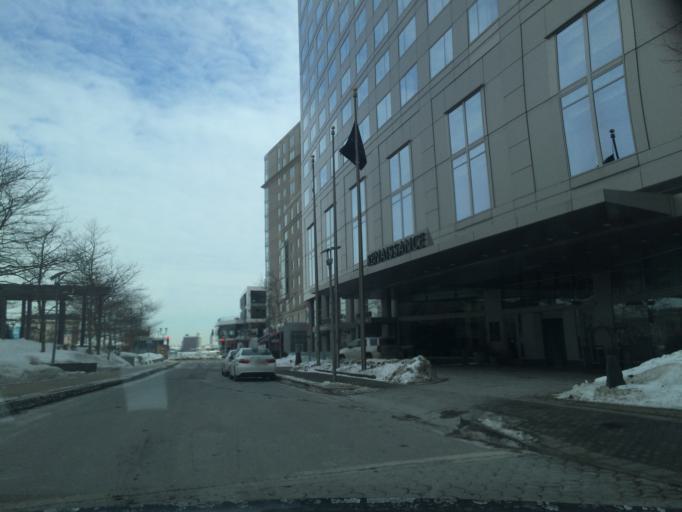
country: US
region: Massachusetts
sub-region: Suffolk County
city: South Boston
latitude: 42.3480
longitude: -71.0400
